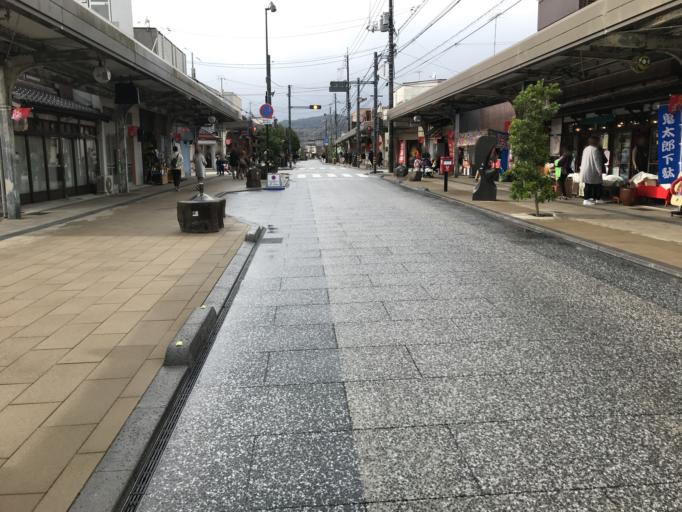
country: JP
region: Shimane
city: Sakaiminato
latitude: 35.5461
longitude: 133.2294
